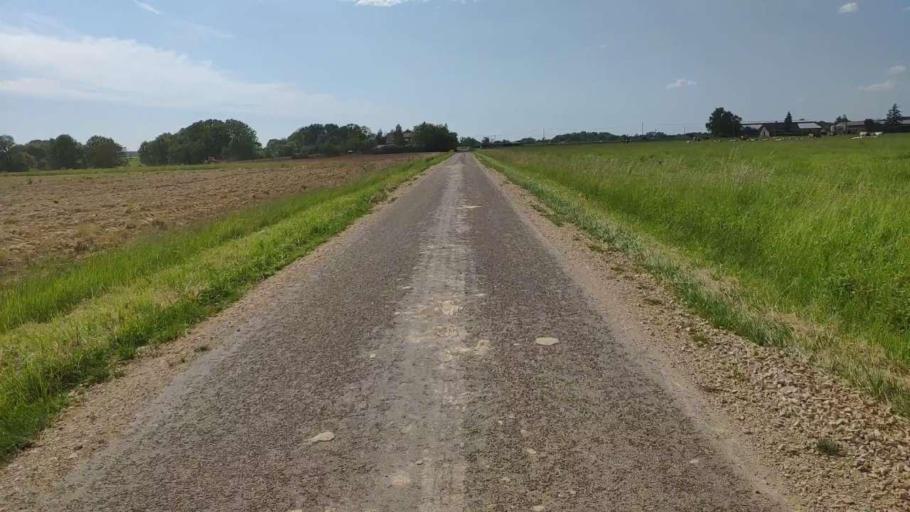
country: FR
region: Franche-Comte
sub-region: Departement du Jura
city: Bletterans
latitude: 46.8125
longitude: 5.3960
